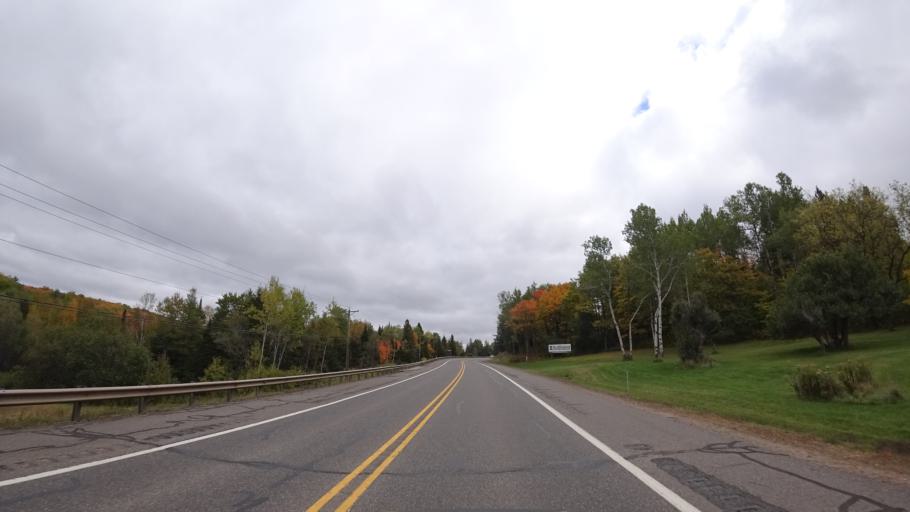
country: US
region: Michigan
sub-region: Marquette County
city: West Ishpeming
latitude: 46.5120
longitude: -87.9619
